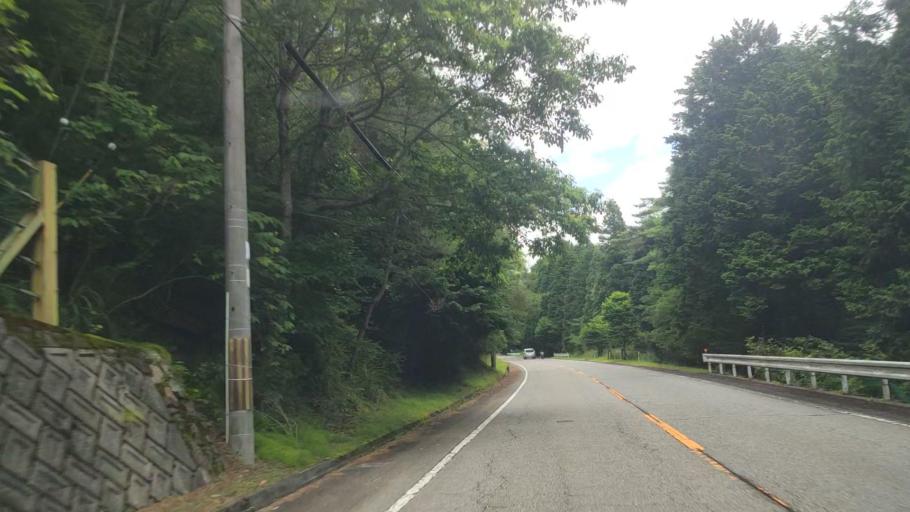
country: JP
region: Kyoto
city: Fukuchiyama
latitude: 35.2086
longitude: 134.9390
